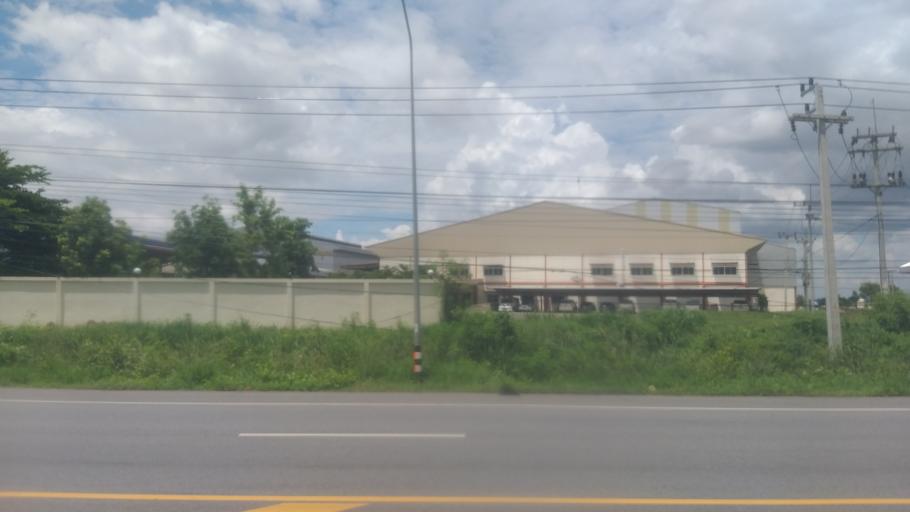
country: TH
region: Nakhon Ratchasima
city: Non Thai
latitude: 15.1061
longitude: 102.1023
